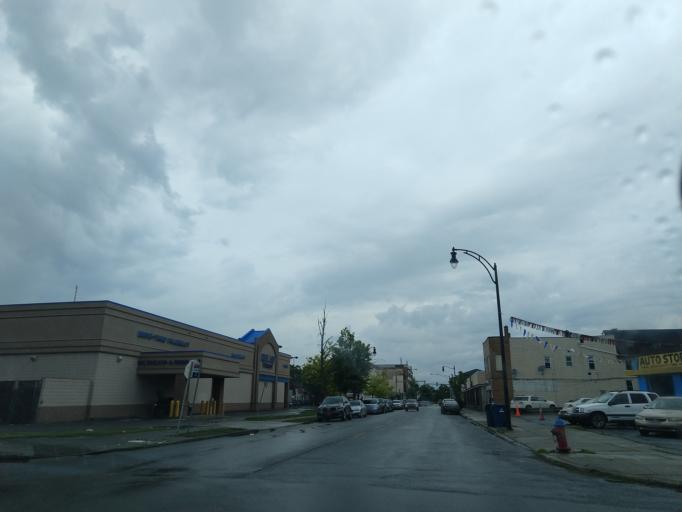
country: US
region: New York
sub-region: Erie County
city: Buffalo
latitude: 42.9140
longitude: -78.8902
